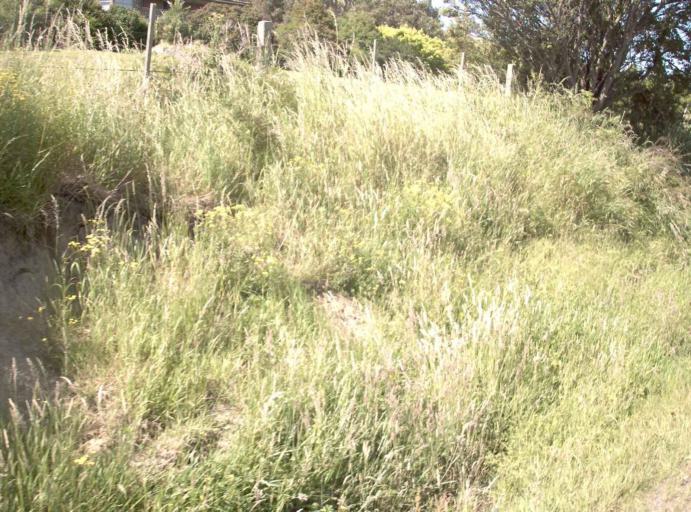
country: AU
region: Victoria
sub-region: Latrobe
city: Morwell
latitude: -38.6664
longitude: 146.3445
